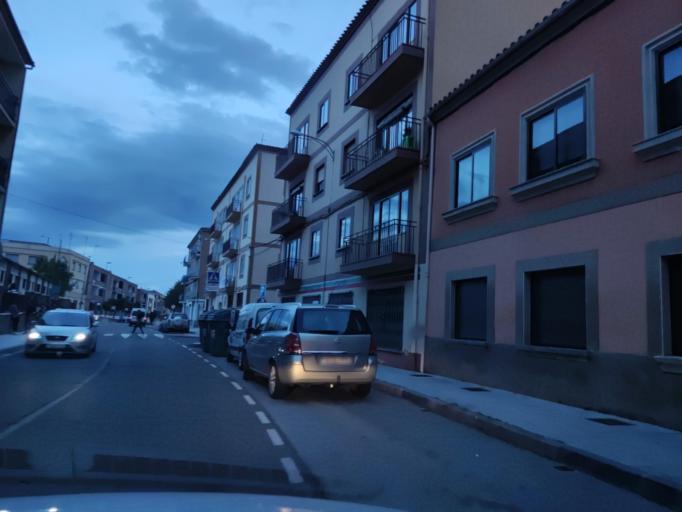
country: ES
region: Castille and Leon
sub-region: Provincia de Salamanca
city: Ciudad Rodrigo
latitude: 40.5975
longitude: -6.5289
